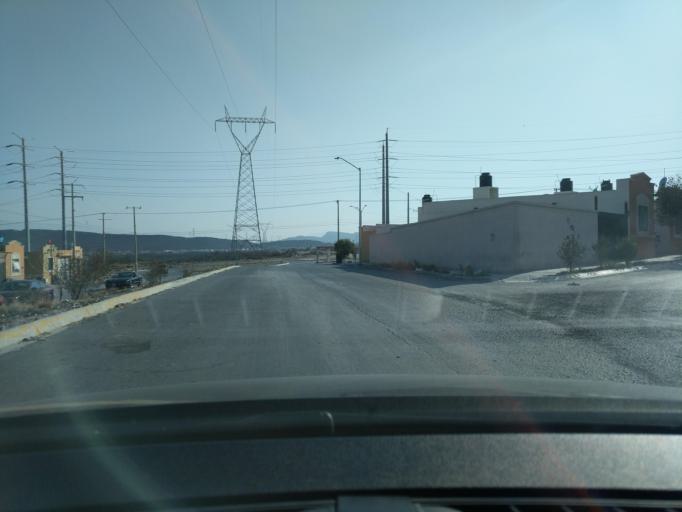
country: MX
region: Coahuila
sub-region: Ramos Arizpe
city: Ramos Arizpe
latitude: 25.5433
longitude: -100.9705
